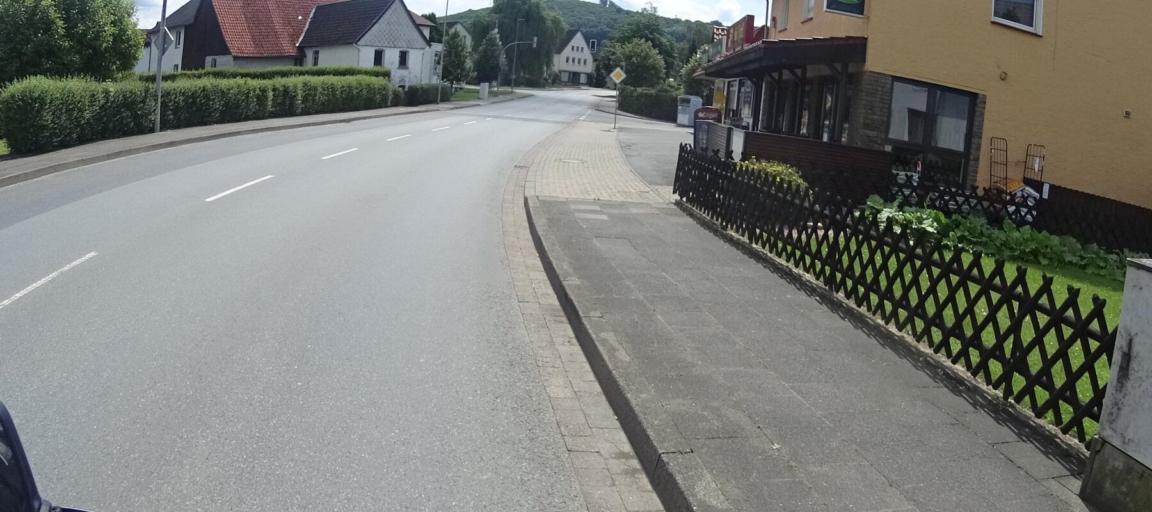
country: DE
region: Lower Saxony
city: Vahlbruch
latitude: 51.8802
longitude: 9.2817
